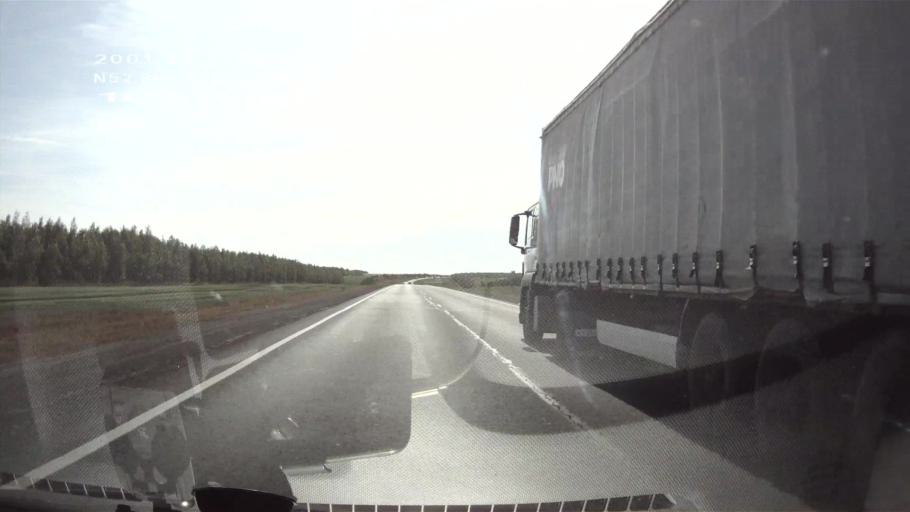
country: RU
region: Samara
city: Syzran'
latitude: 52.8927
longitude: 48.2950
